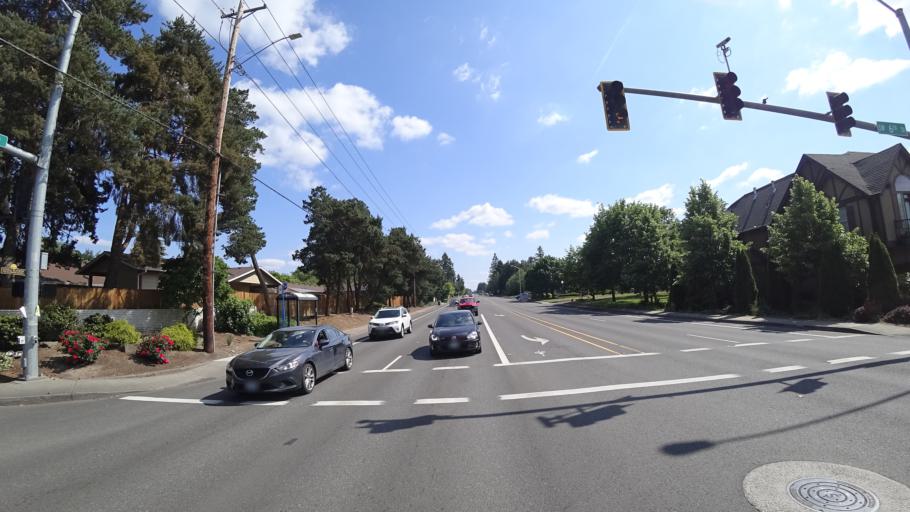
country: US
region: Oregon
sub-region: Washington County
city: Beaverton
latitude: 45.4818
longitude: -122.8261
